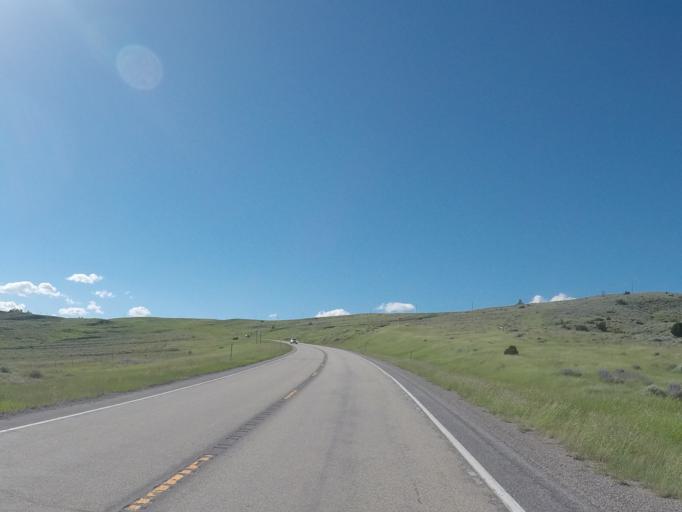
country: US
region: Montana
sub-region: Carbon County
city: Red Lodge
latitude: 45.1776
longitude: -109.2126
